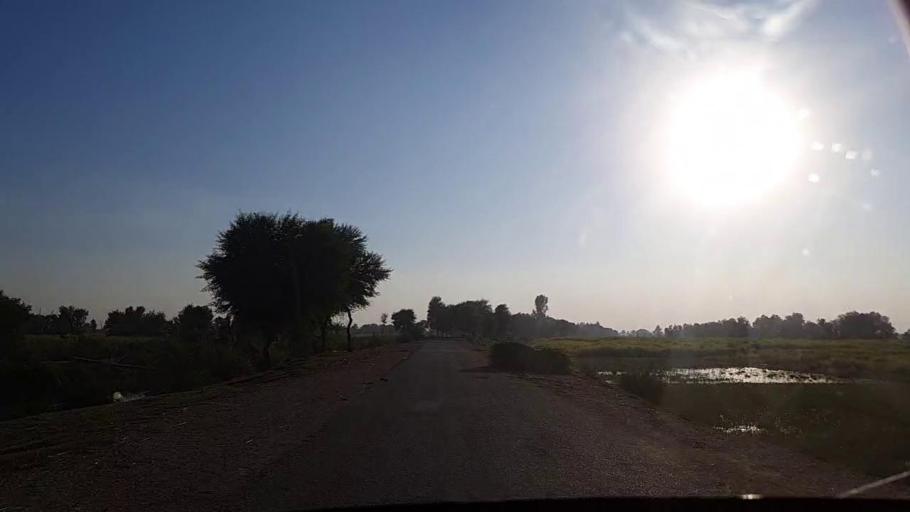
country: PK
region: Sindh
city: Sobhadero
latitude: 27.4194
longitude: 68.4043
